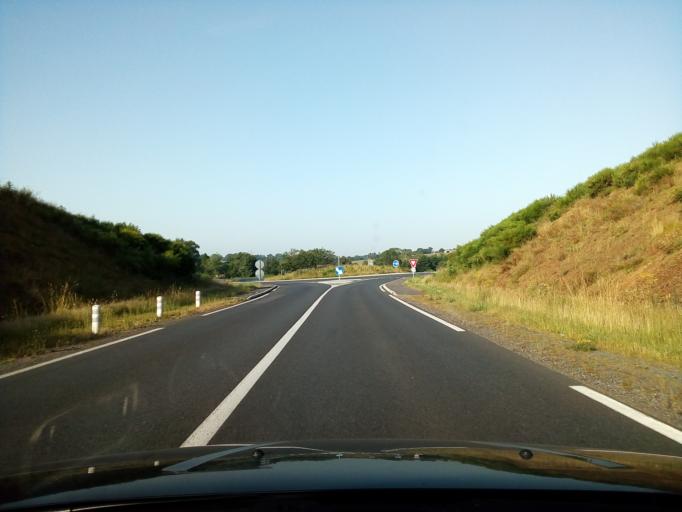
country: FR
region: Limousin
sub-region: Departement de la Haute-Vienne
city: Bussiere-Poitevine
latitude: 46.1099
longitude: 0.8943
